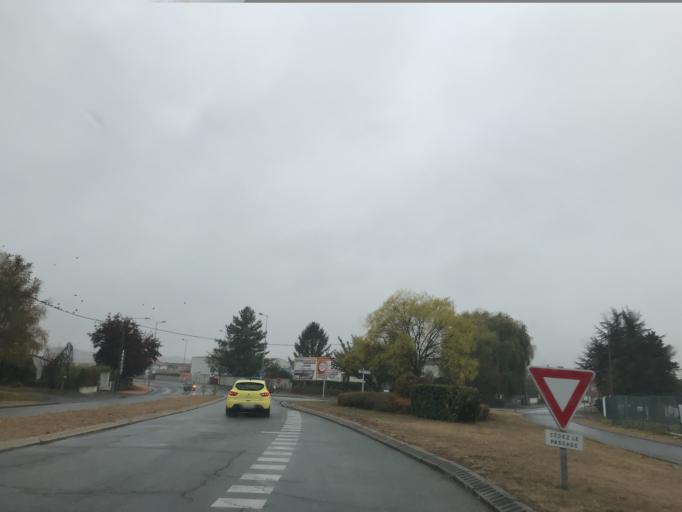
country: FR
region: Auvergne
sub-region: Departement du Puy-de-Dome
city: Dallet
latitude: 45.7771
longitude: 3.2026
